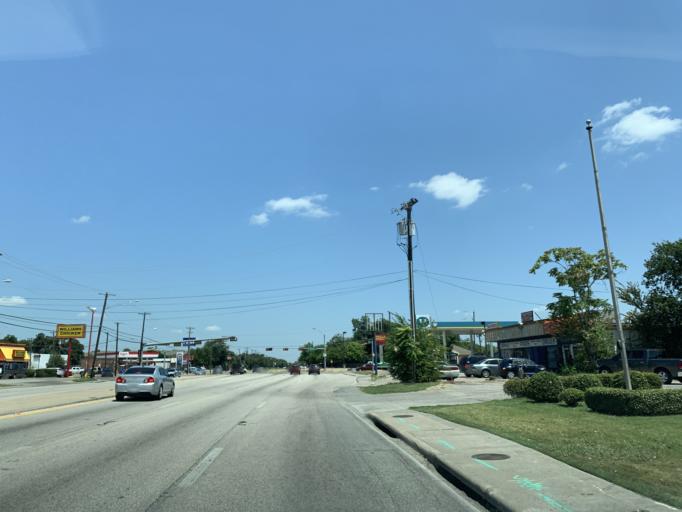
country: US
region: Texas
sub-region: Dallas County
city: Hutchins
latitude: 32.6939
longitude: -96.7732
